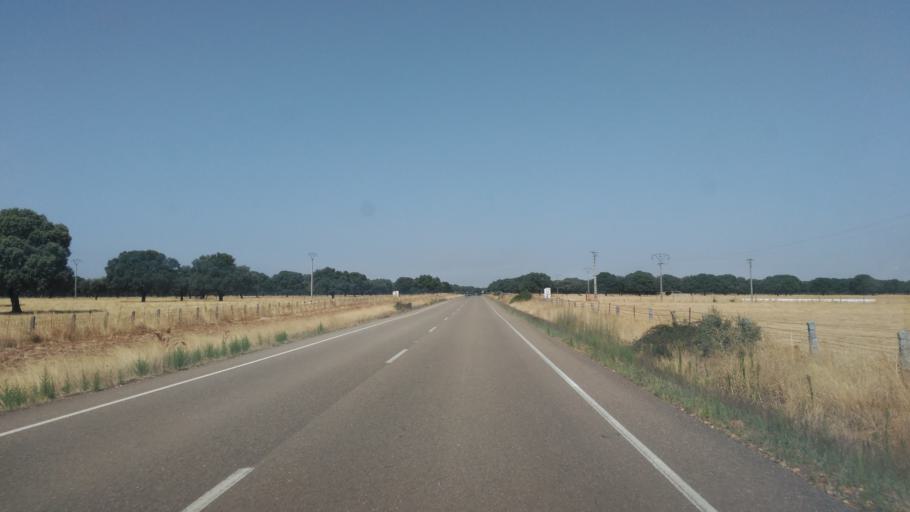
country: ES
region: Castille and Leon
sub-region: Provincia de Salamanca
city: Tamames
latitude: 40.6780
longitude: -6.1267
